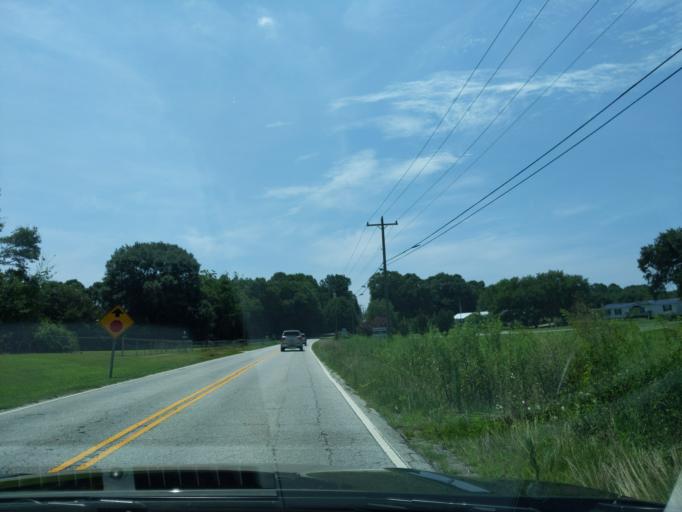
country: US
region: South Carolina
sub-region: Greenville County
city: Five Forks
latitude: 34.7654
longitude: -82.2037
